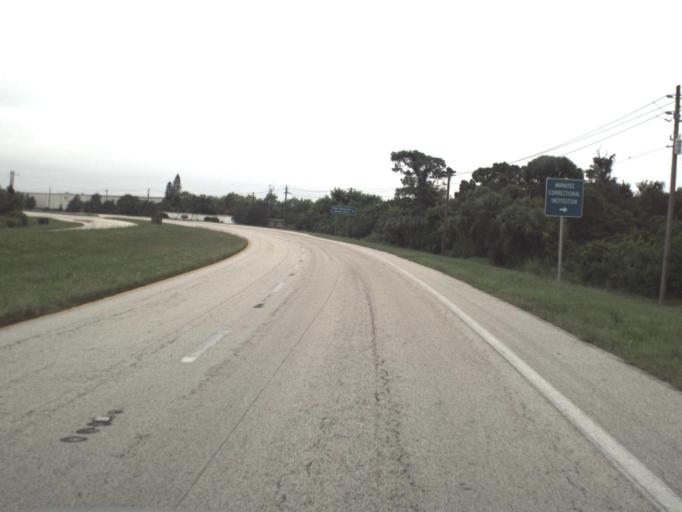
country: US
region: Florida
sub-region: Manatee County
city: Memphis
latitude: 27.6362
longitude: -82.5386
